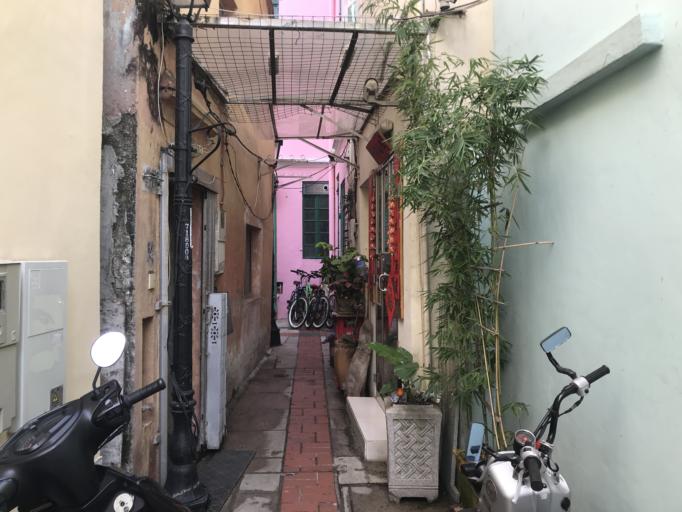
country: MO
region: Macau
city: Macau
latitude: 22.1535
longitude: 113.5567
